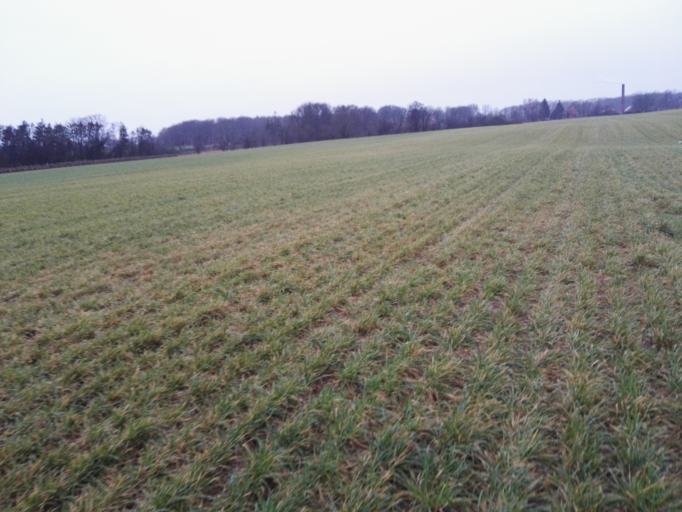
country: DK
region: Capital Region
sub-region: Frederikssund Kommune
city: Jaegerspris
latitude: 55.8510
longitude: 11.9712
